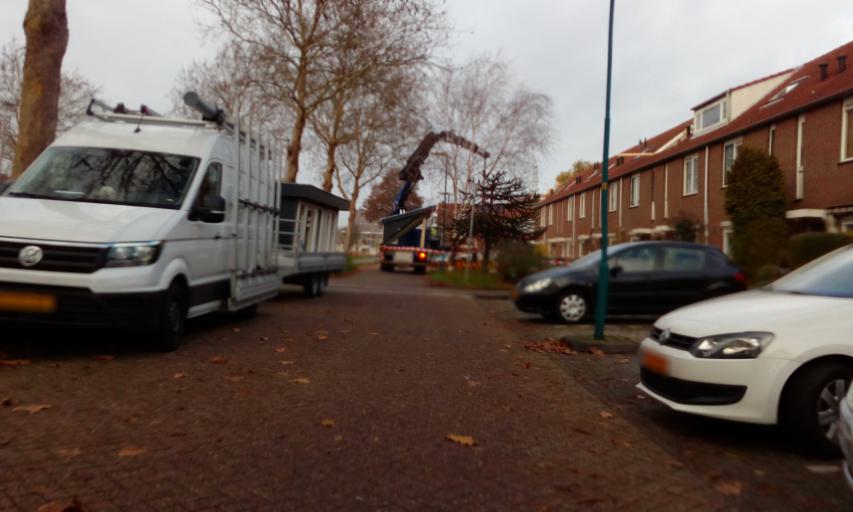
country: NL
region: South Holland
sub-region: Gemeente Zoetermeer
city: Zoetermeer
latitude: 52.0436
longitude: 4.4957
